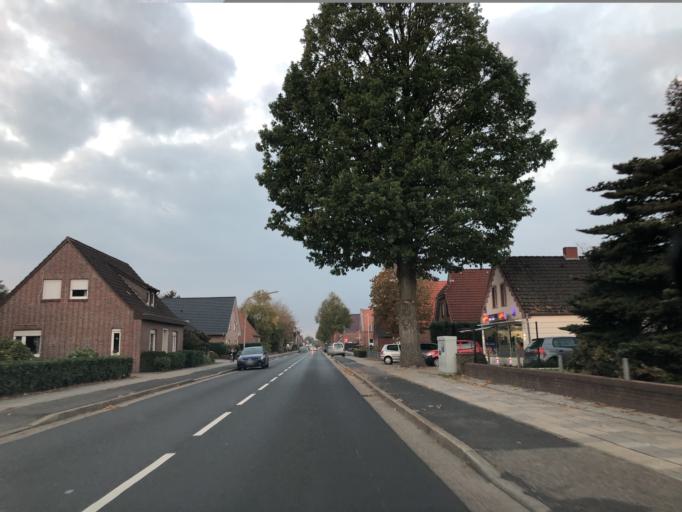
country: DE
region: Lower Saxony
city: Papenburg
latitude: 53.0728
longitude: 7.4227
